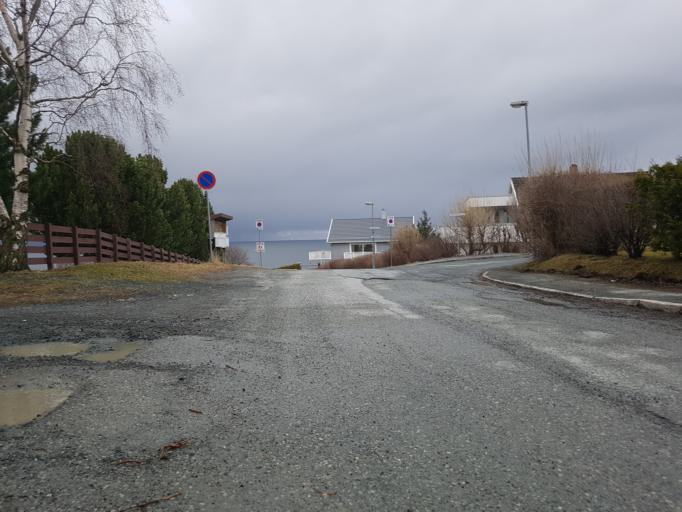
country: NO
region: Sor-Trondelag
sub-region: Trondheim
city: Trondheim
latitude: 63.4297
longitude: 10.5372
